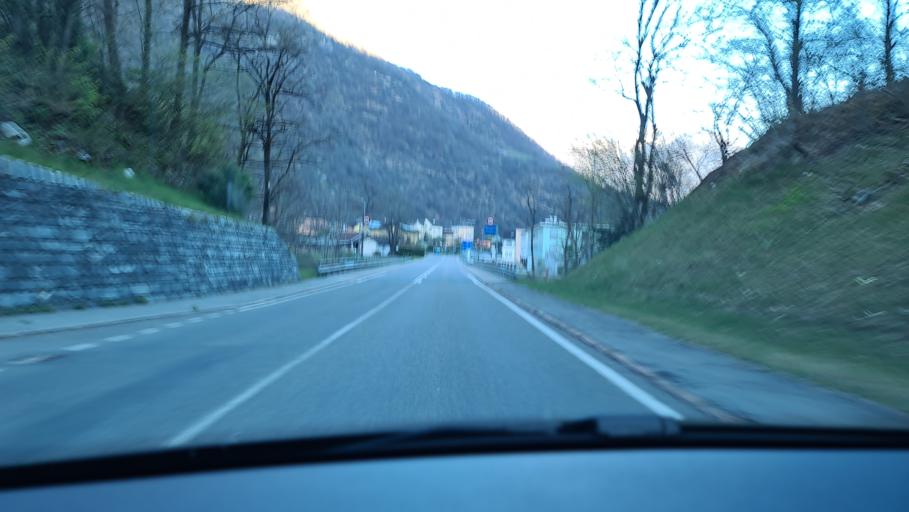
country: CH
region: Ticino
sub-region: Locarno District
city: Verscio
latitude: 46.2465
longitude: 8.7021
